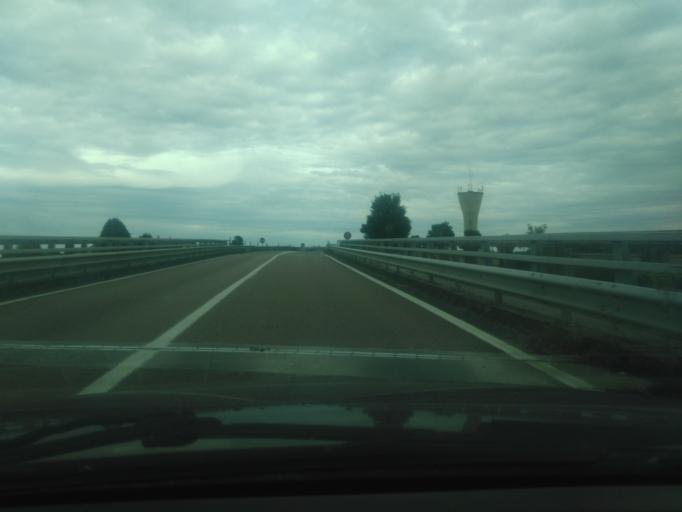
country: FR
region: Bourgogne
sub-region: Departement de la Nievre
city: Saint-Pierre-le-Moutier
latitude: 46.8030
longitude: 3.1193
